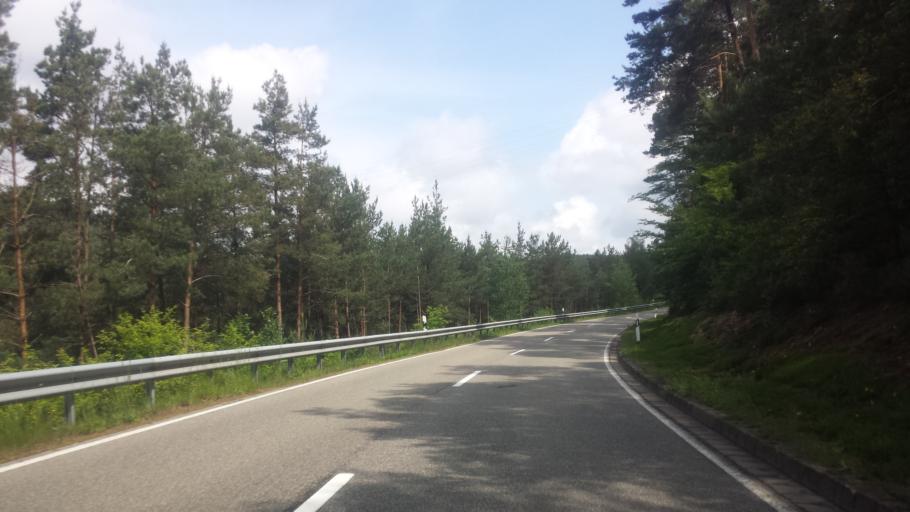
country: DE
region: Rheinland-Pfalz
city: Lindenberg
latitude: 49.3893
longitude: 8.1003
